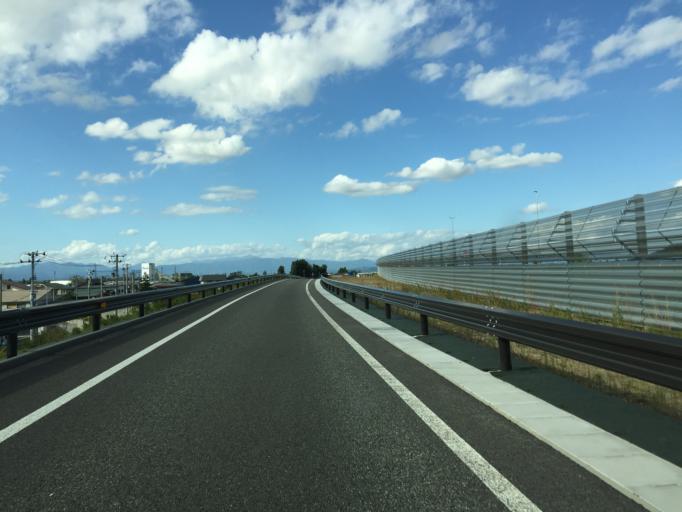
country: JP
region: Yamagata
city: Yonezawa
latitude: 37.9186
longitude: 140.1362
